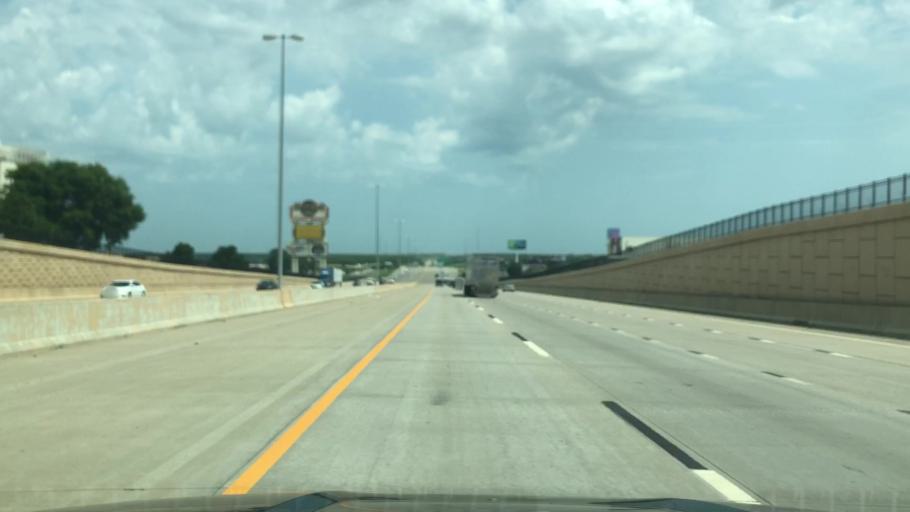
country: US
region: Oklahoma
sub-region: Rogers County
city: Catoosa
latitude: 36.1629
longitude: -95.7701
